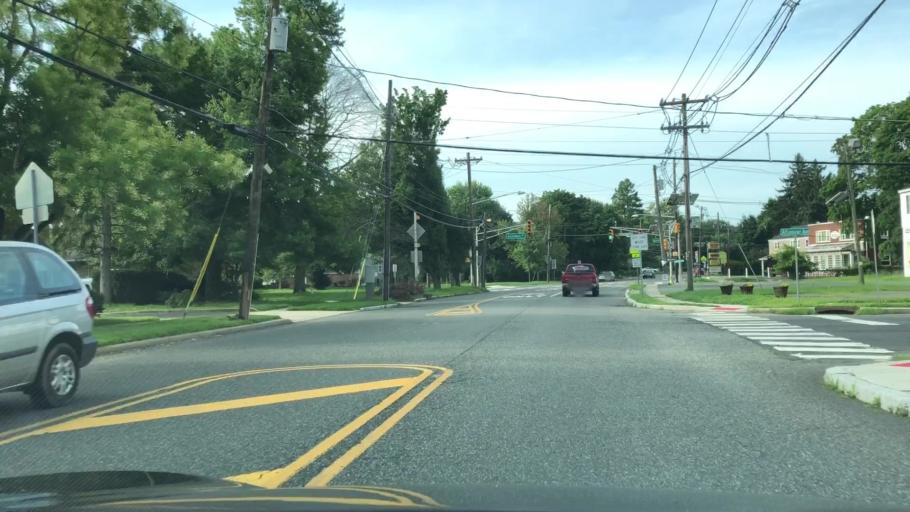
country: US
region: New Jersey
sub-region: Mercer County
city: Lawrenceville
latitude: 40.2648
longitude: -74.7405
